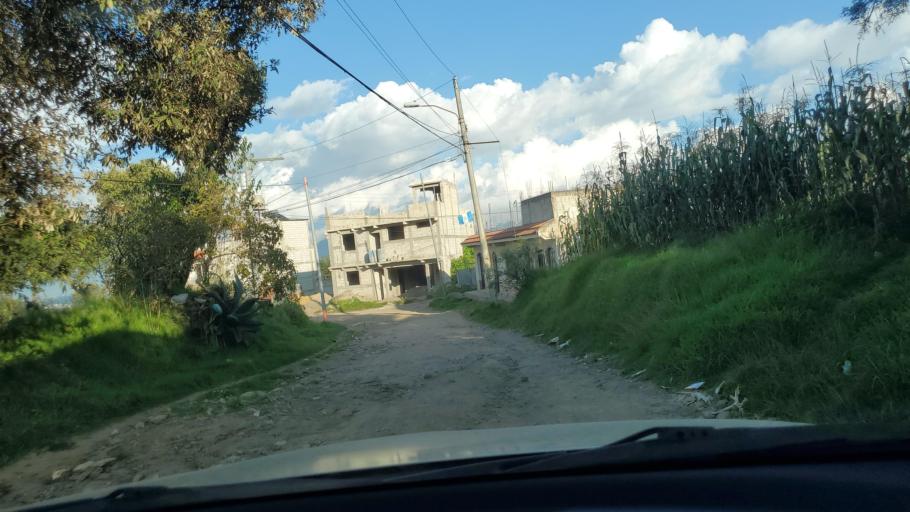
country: GT
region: Quetzaltenango
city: Quetzaltenango
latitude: 14.8367
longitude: -91.5480
